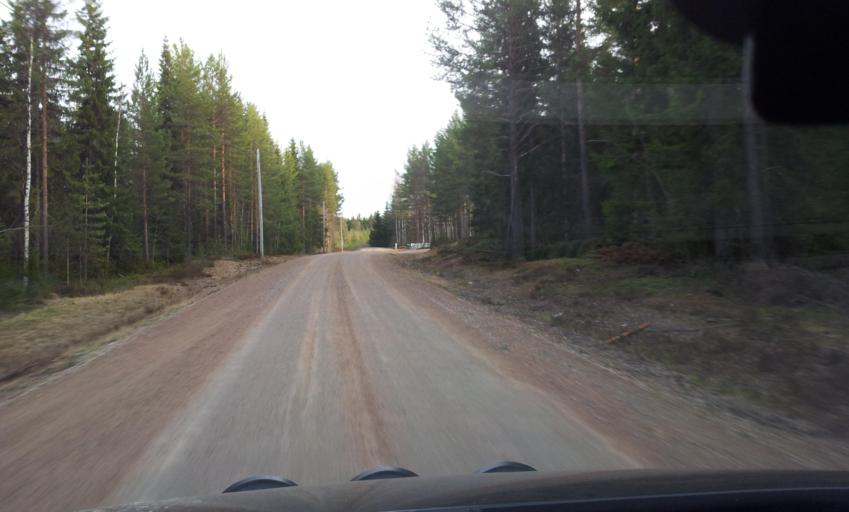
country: SE
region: Gaevleborg
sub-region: Ljusdals Kommun
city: Farila
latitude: 62.1360
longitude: 15.6612
